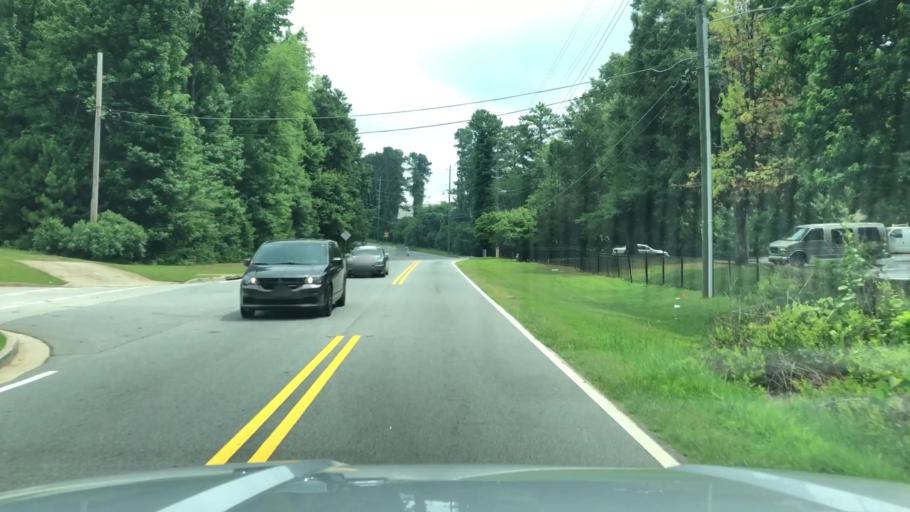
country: US
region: Georgia
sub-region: Cobb County
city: Mableton
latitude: 33.7762
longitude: -84.5773
